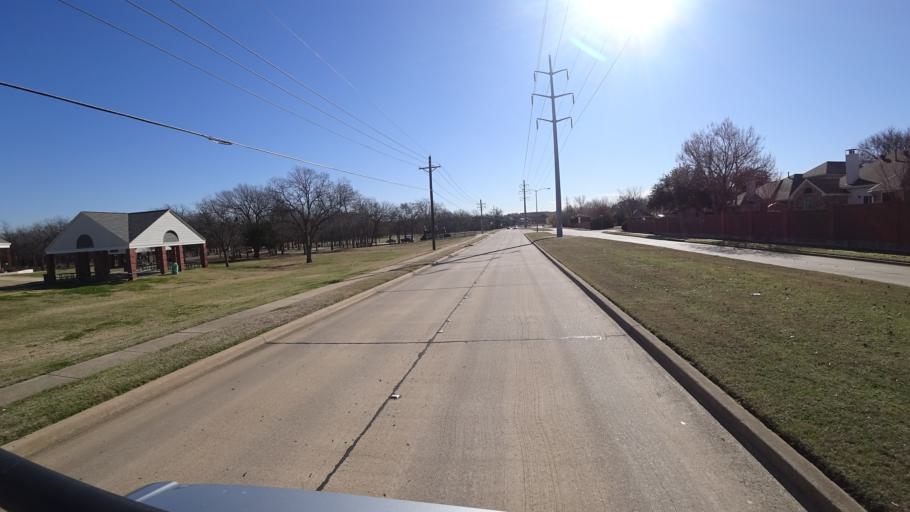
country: US
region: Texas
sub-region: Denton County
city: Lewisville
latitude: 33.0174
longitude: -97.0062
